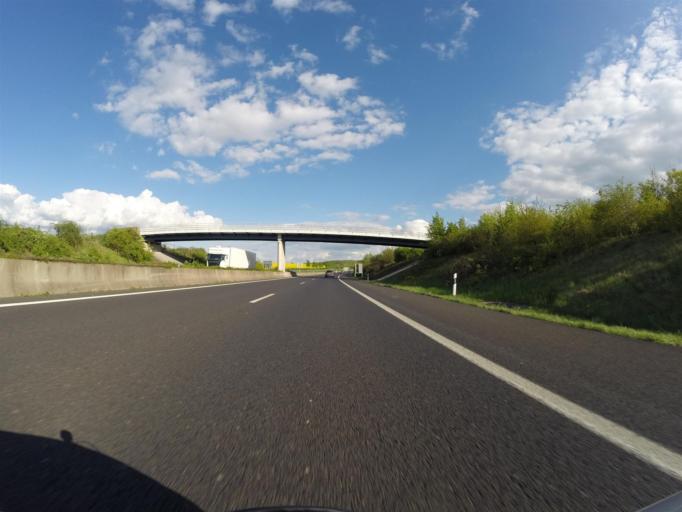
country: LU
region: Grevenmacher
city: Schengen
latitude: 49.4911
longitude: 6.3285
